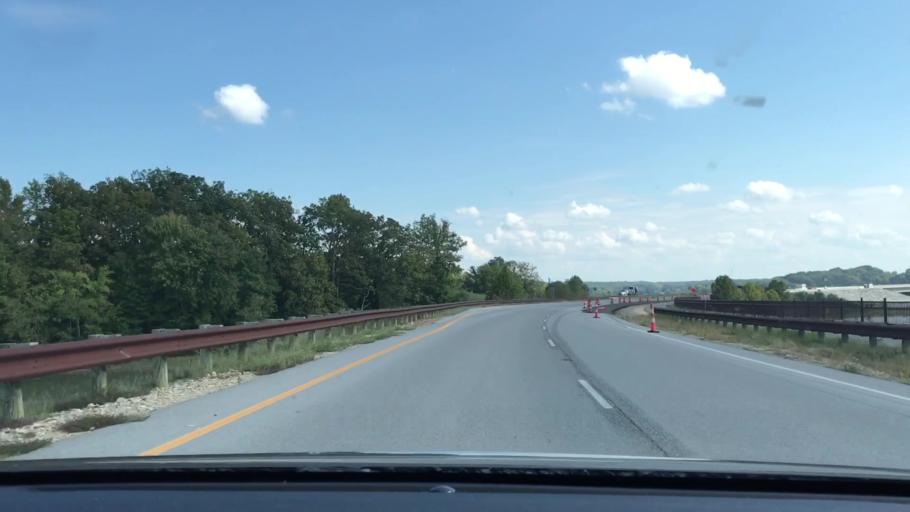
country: US
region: Kentucky
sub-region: Trigg County
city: Cadiz
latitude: 36.8014
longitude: -87.9886
